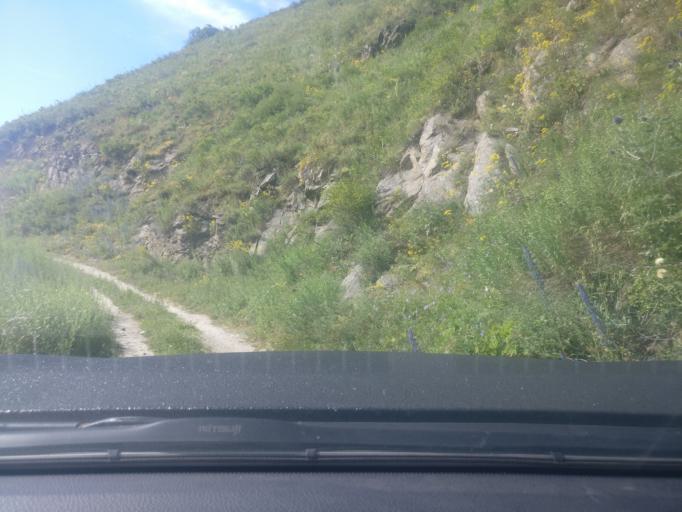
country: KZ
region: Almaty Qalasy
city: Almaty
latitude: 43.0989
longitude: 76.9534
